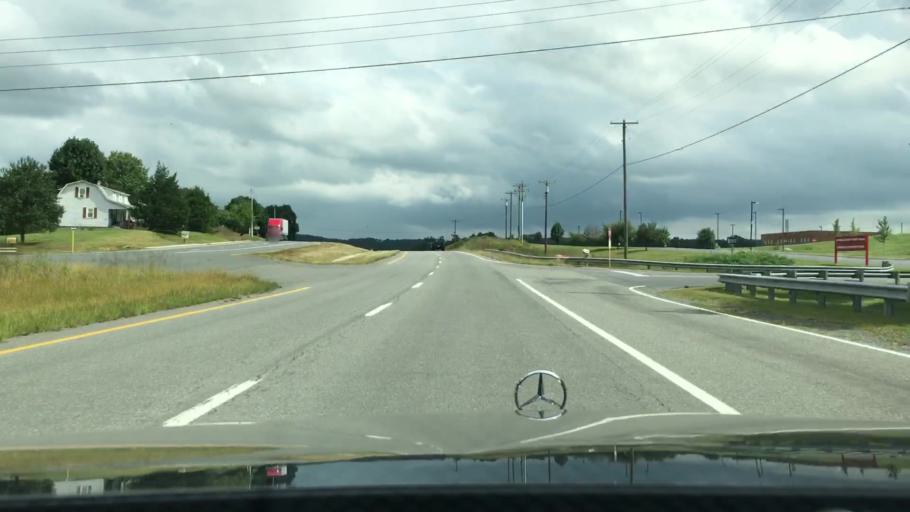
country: US
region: Virginia
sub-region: City of Winchester
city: Winchester
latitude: 39.2723
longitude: -78.2497
